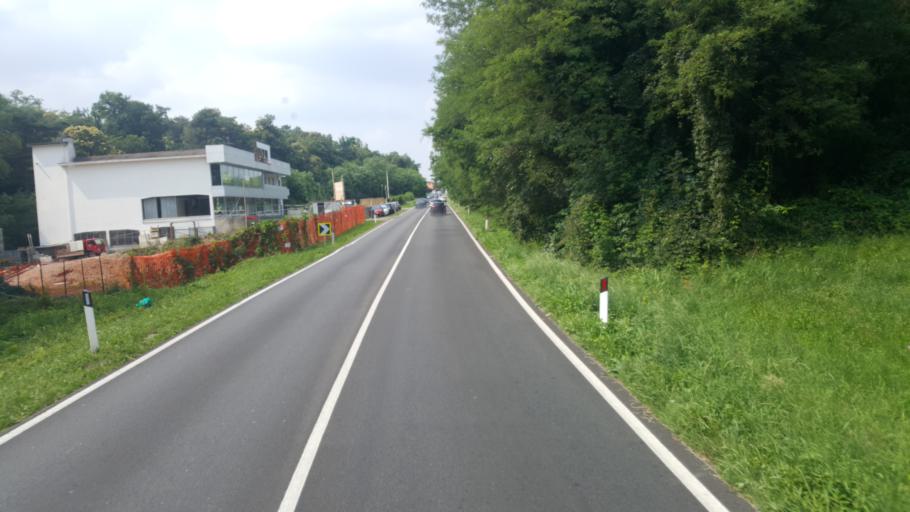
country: IT
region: Lombardy
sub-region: Provincia di Como
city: Beregazzo
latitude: 45.7628
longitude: 8.9621
